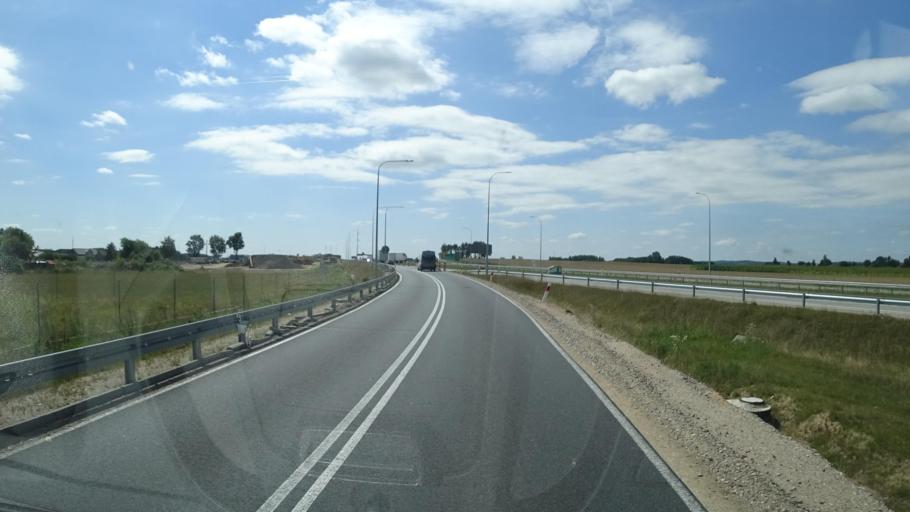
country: PL
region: Podlasie
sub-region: Powiat grajewski
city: Szczuczyn
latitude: 53.5881
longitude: 22.3285
